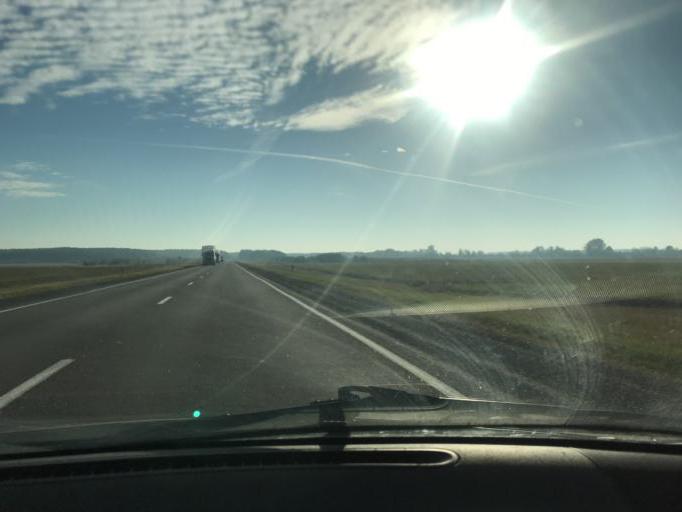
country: BY
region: Brest
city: Drahichyn
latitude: 52.1902
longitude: 25.2691
